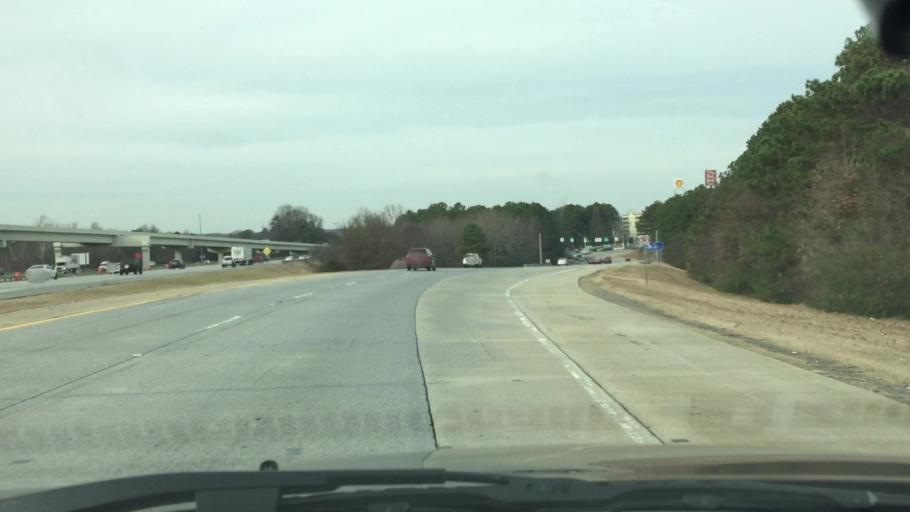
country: US
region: Georgia
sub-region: Cobb County
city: Kennesaw
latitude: 34.0065
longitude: -84.5654
